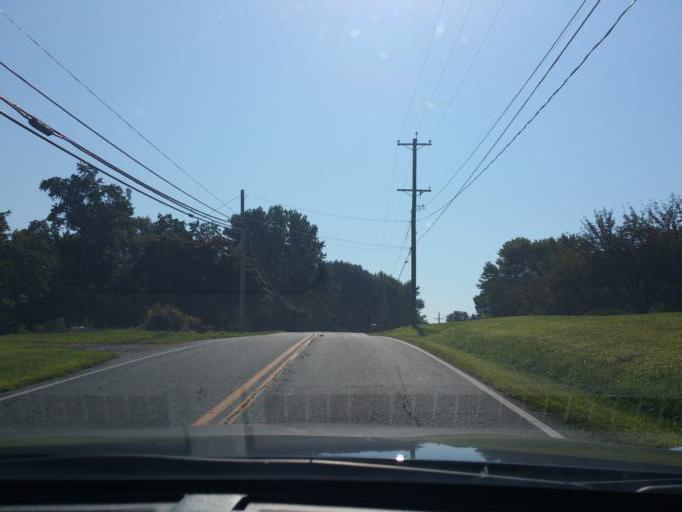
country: US
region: Maryland
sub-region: Cecil County
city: Rising Sun
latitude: 39.6498
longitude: -76.1405
